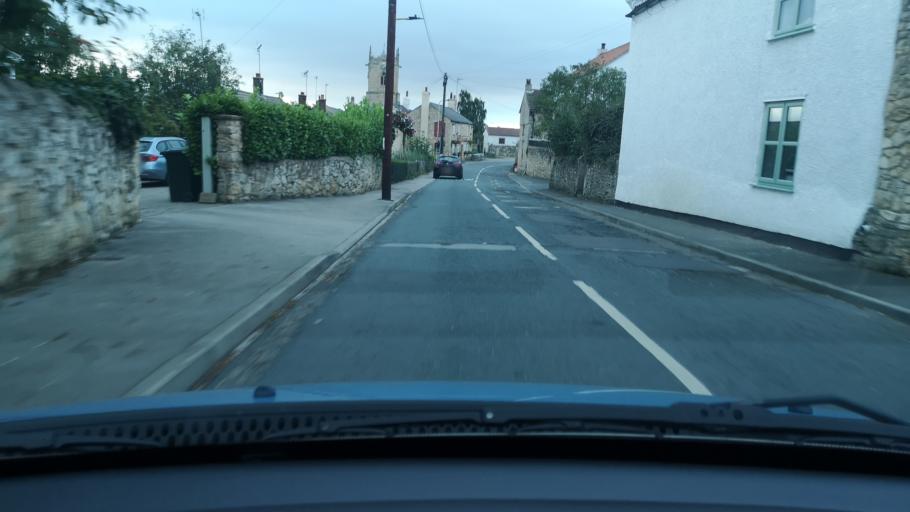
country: GB
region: England
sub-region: Doncaster
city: Norton
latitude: 53.6439
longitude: -1.2171
